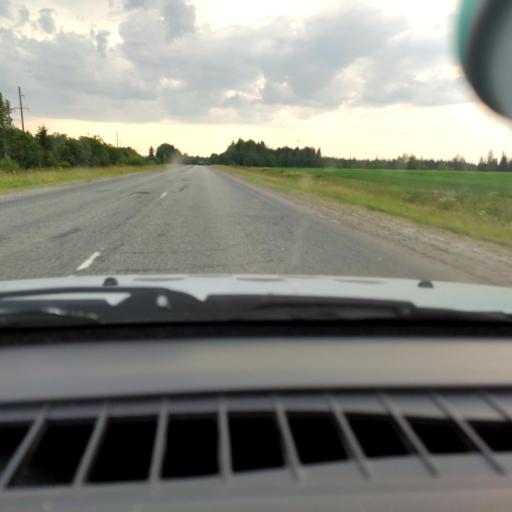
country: RU
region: Udmurtiya
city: Debesy
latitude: 57.6053
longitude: 53.4750
